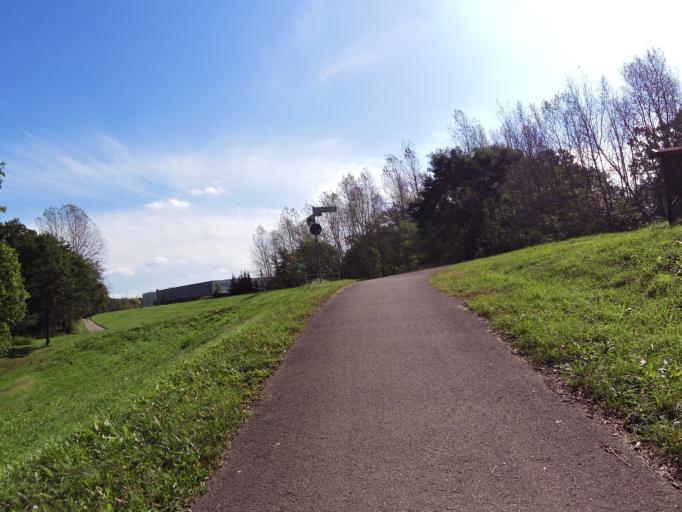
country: DE
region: Saxony-Anhalt
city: Dessau
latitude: 51.8591
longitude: 12.2385
